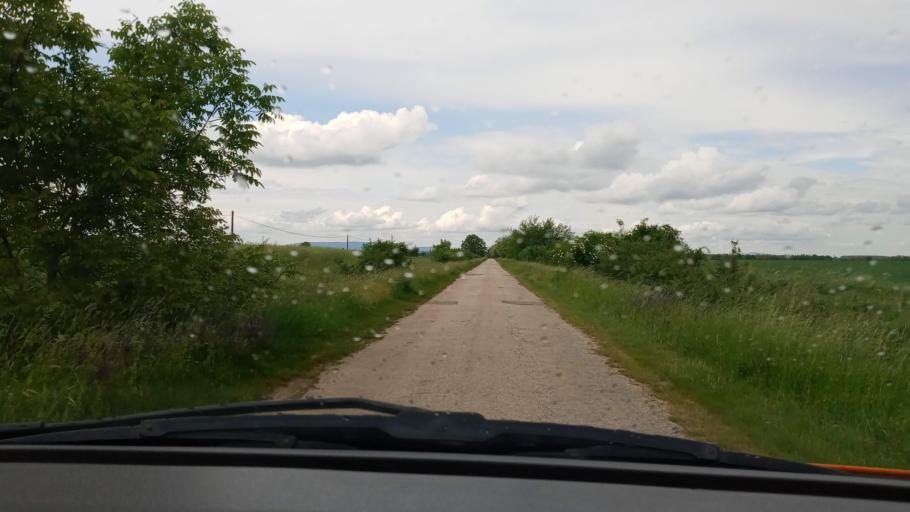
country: HU
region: Baranya
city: Harkany
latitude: 45.9062
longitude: 18.1385
